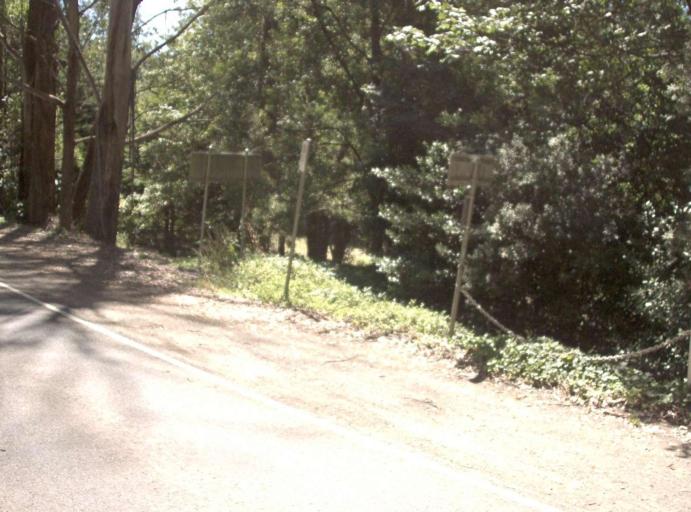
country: AU
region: Victoria
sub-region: Yarra Ranges
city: Olinda
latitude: -37.8570
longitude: 145.3667
